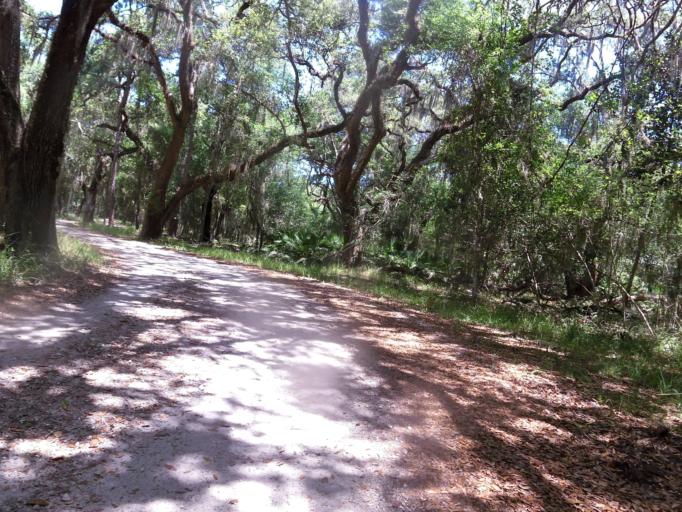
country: US
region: Florida
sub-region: Saint Johns County
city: Villano Beach
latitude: 30.0306
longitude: -81.3374
